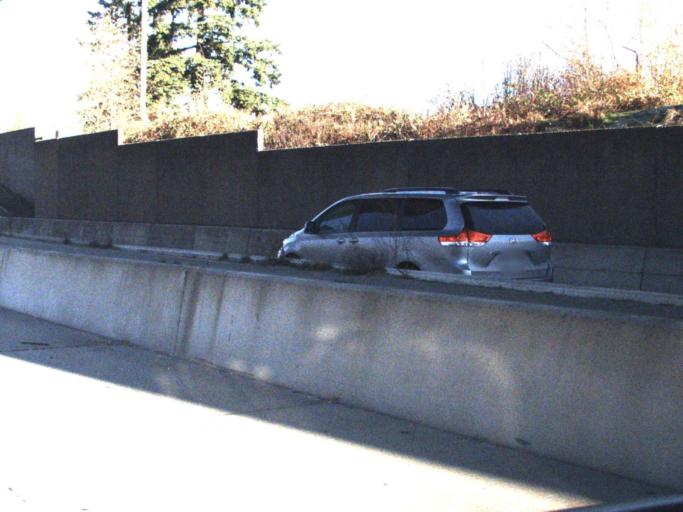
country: US
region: Washington
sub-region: Snohomish County
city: Everett
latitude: 47.9611
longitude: -122.1993
